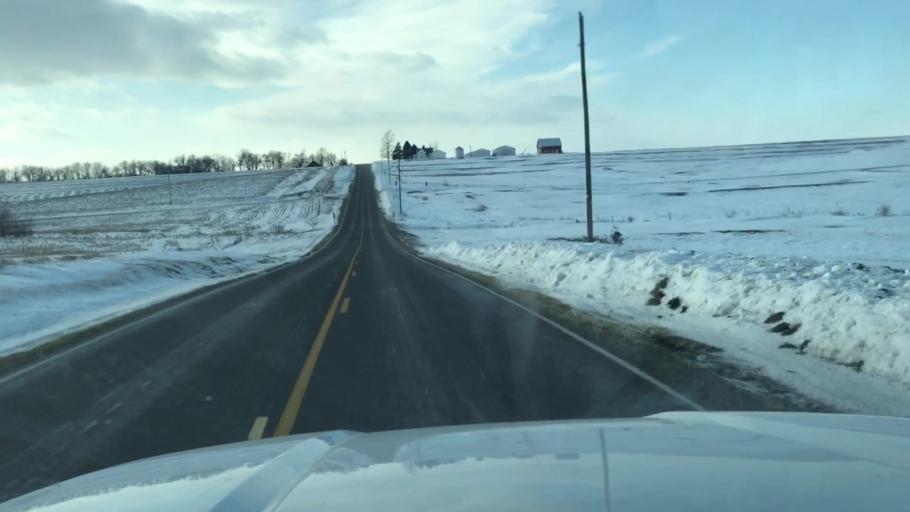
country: US
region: Missouri
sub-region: Nodaway County
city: Maryville
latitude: 40.2012
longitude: -94.9130
